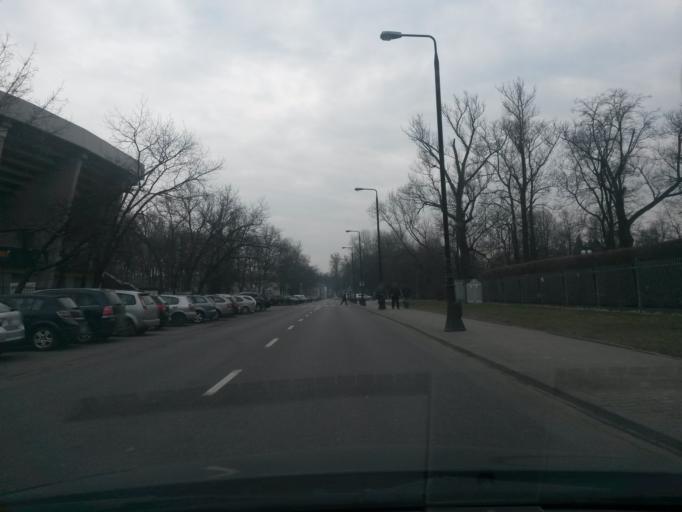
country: PL
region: Masovian Voivodeship
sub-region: Warszawa
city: Srodmiescie
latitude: 52.2202
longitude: 21.0364
